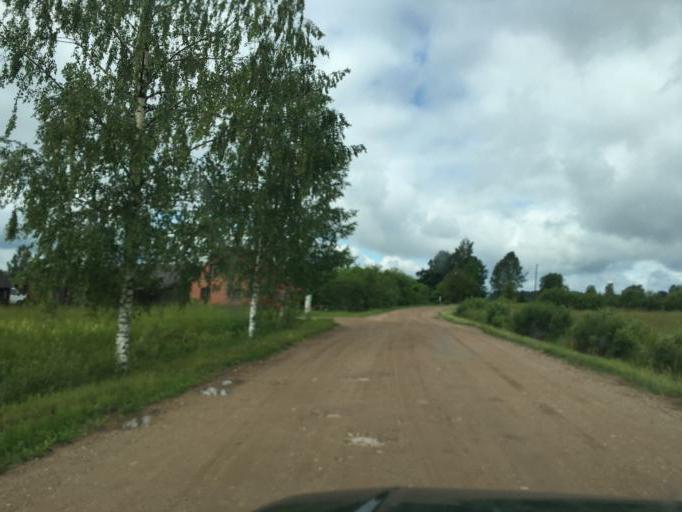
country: LV
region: Balvu Rajons
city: Balvi
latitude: 57.2137
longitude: 27.3145
